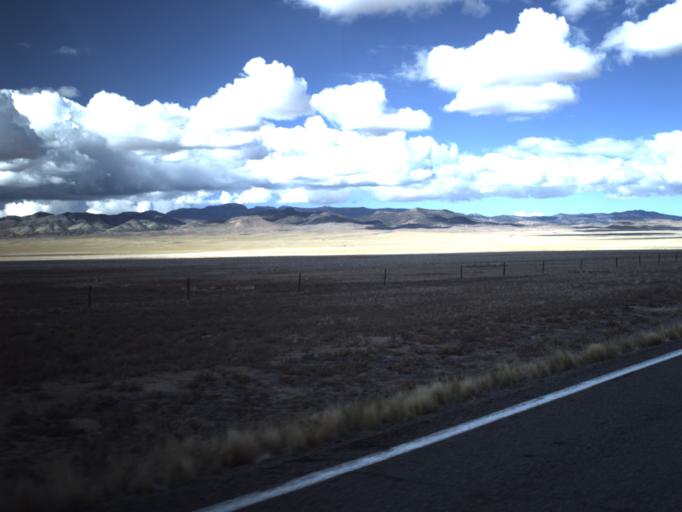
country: US
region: Utah
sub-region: Beaver County
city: Milford
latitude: 38.5505
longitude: -113.7310
